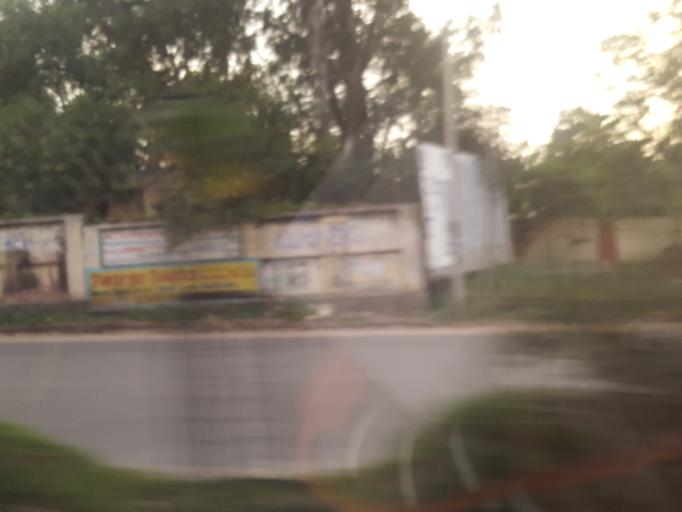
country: IN
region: Telangana
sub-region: Rangareddi
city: Kukatpalli
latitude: 17.5126
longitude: 78.3612
